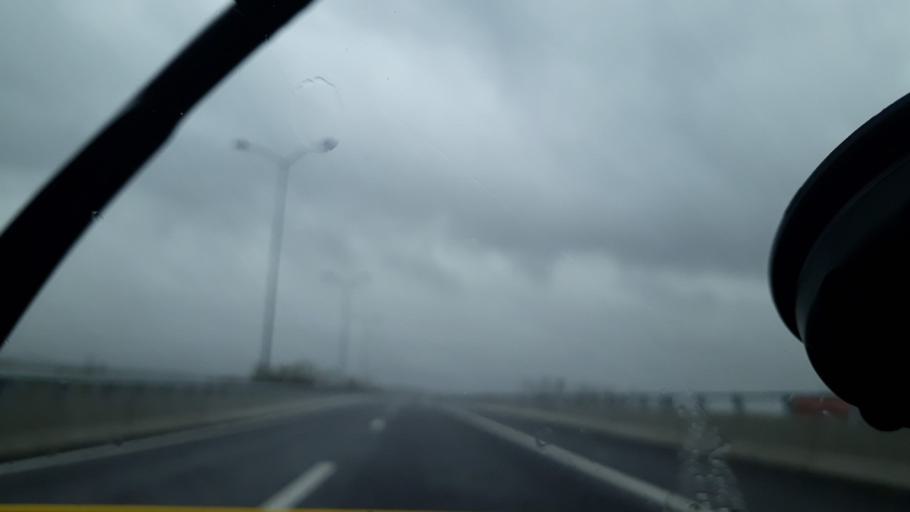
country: BA
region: Republika Srpska
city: Maglajani
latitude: 44.9143
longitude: 17.3393
